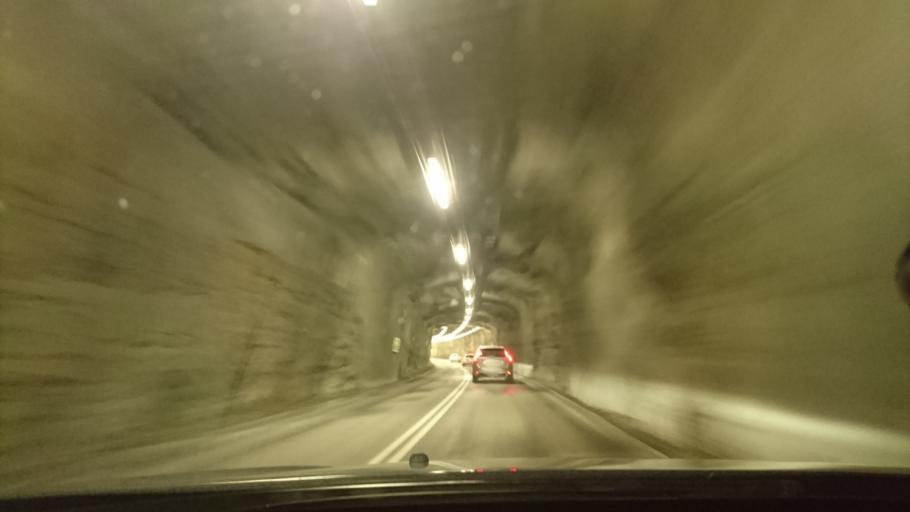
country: SE
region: Stockholm
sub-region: Nynashamns Kommun
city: Nynashamn
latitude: 58.9704
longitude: 18.0562
